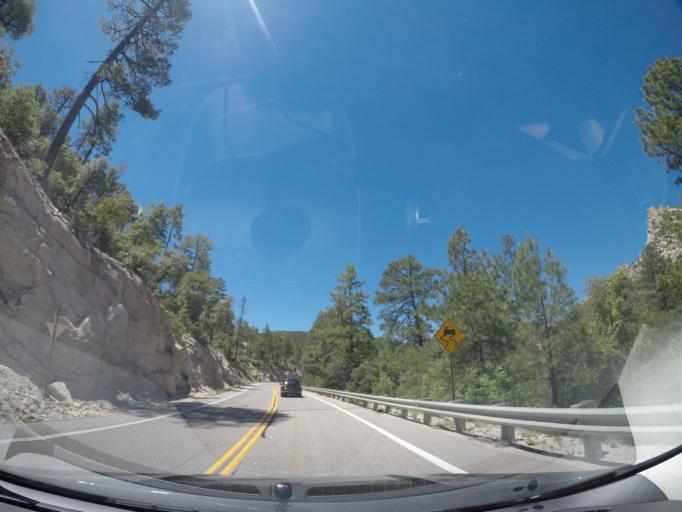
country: US
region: Arizona
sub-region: Pima County
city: Tanque Verde
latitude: 32.3761
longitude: -110.6883
